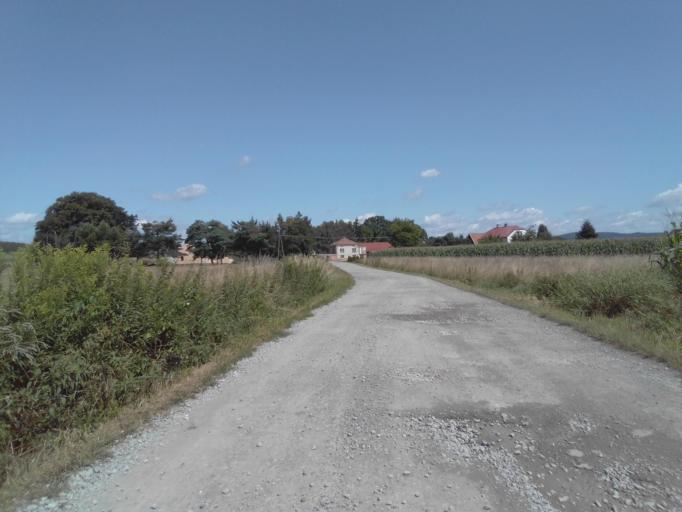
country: PL
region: Subcarpathian Voivodeship
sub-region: Powiat krosnienski
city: Wojaszowka
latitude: 49.7653
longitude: 21.6435
